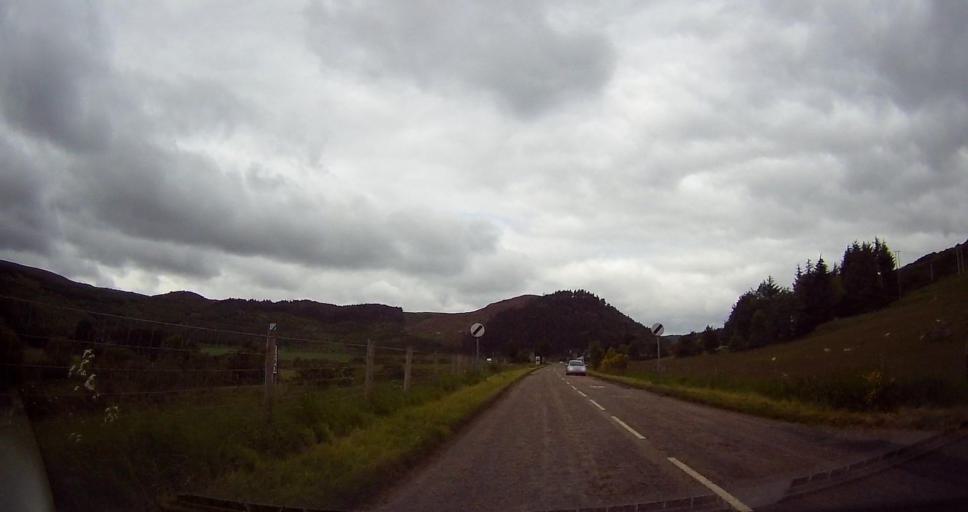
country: GB
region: Scotland
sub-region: Highland
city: Dornoch
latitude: 57.9914
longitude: -4.1649
